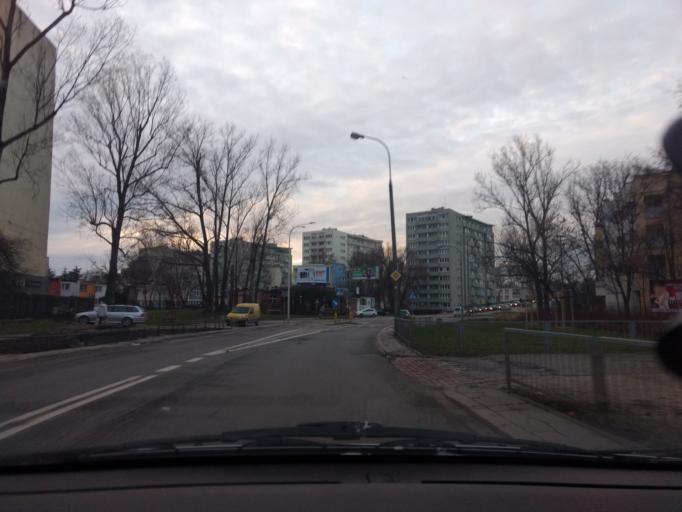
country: PL
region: Masovian Voivodeship
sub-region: Warszawa
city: Praga Poludnie
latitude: 52.2267
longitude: 21.0650
